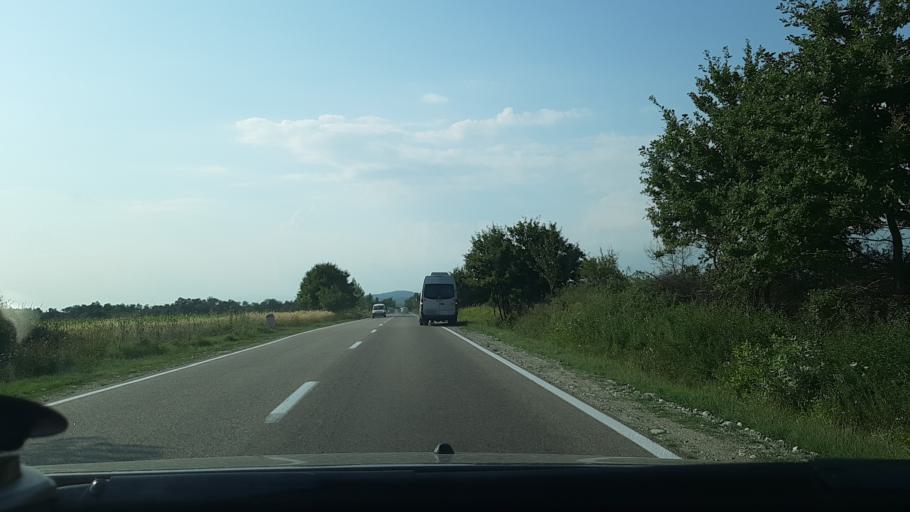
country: RO
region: Gorj
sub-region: Comuna Targu Carbunesti
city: Pojogeni
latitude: 45.0042
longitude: 23.4866
